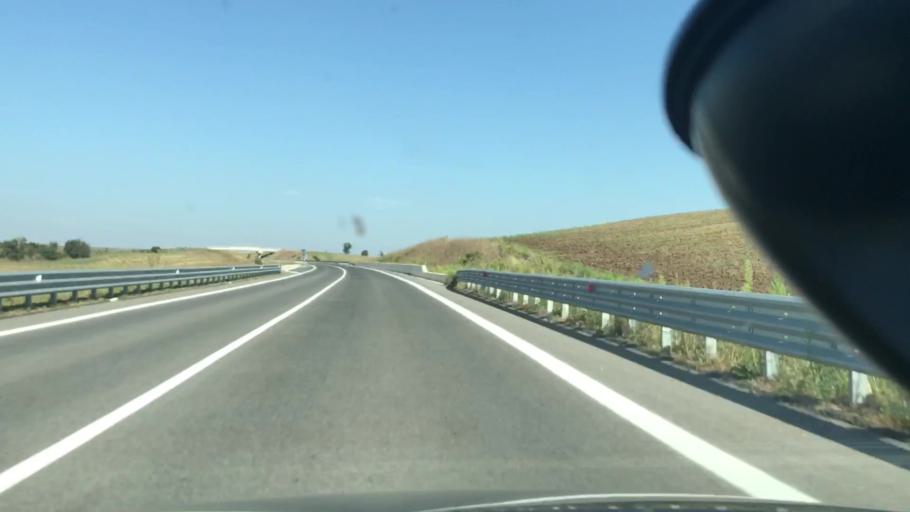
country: IT
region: Basilicate
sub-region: Provincia di Potenza
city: Palazzo San Gervasio
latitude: 40.9643
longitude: 16.0100
